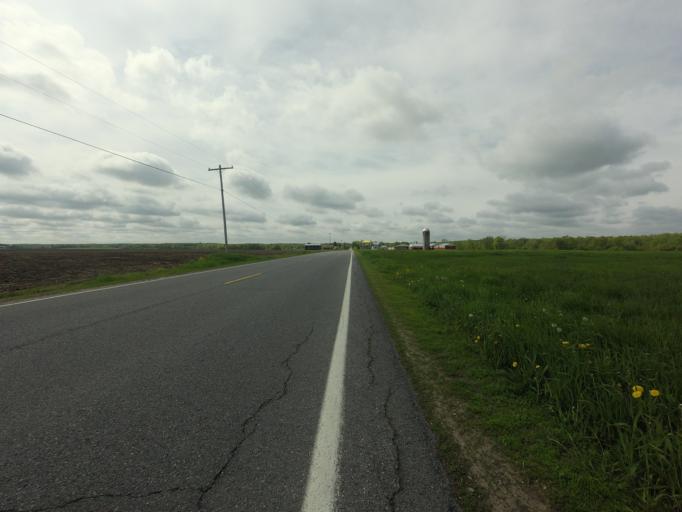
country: CA
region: Ontario
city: Cornwall
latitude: 44.7637
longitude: -74.6707
